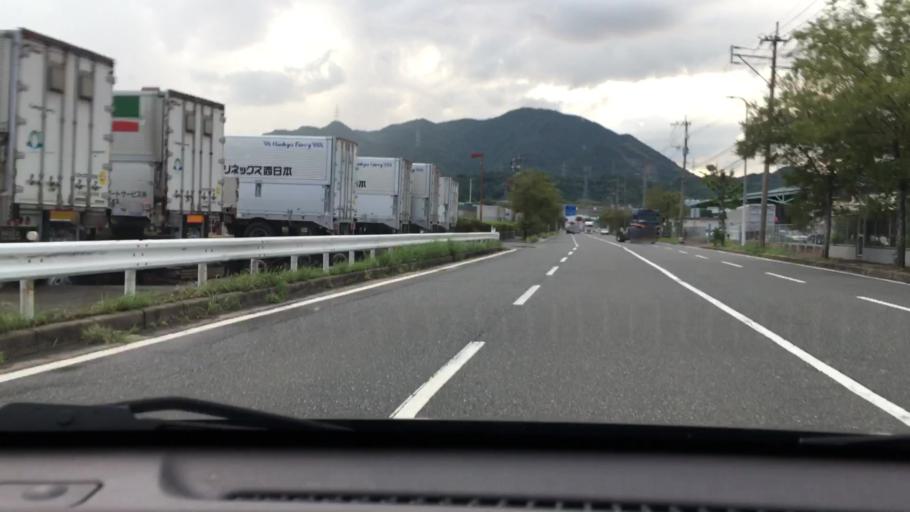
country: JP
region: Yamaguchi
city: Shimonoseki
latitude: 33.8864
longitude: 130.9920
